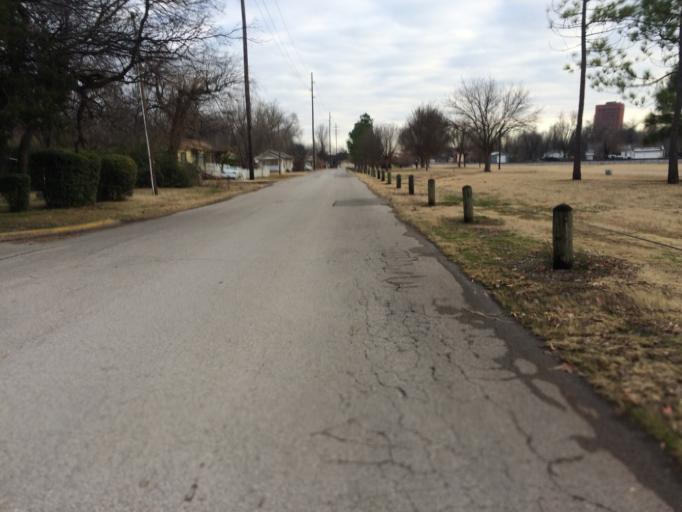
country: US
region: Oklahoma
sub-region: Cleveland County
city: Norman
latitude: 35.2176
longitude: -97.4411
